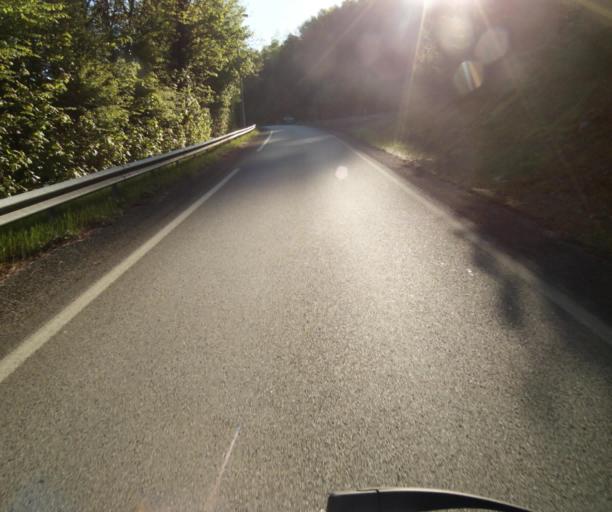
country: FR
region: Limousin
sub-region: Departement de la Correze
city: Laguenne
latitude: 45.2497
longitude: 1.7734
